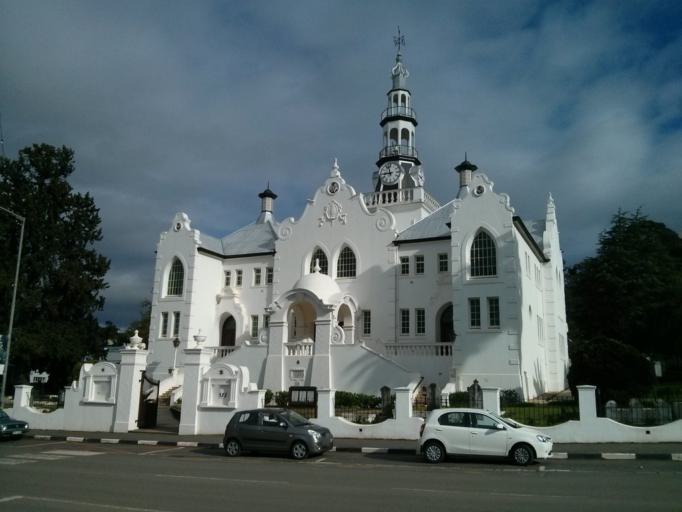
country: ZA
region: Western Cape
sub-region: Overberg District Municipality
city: Swellendam
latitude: -34.0135
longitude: 20.4501
